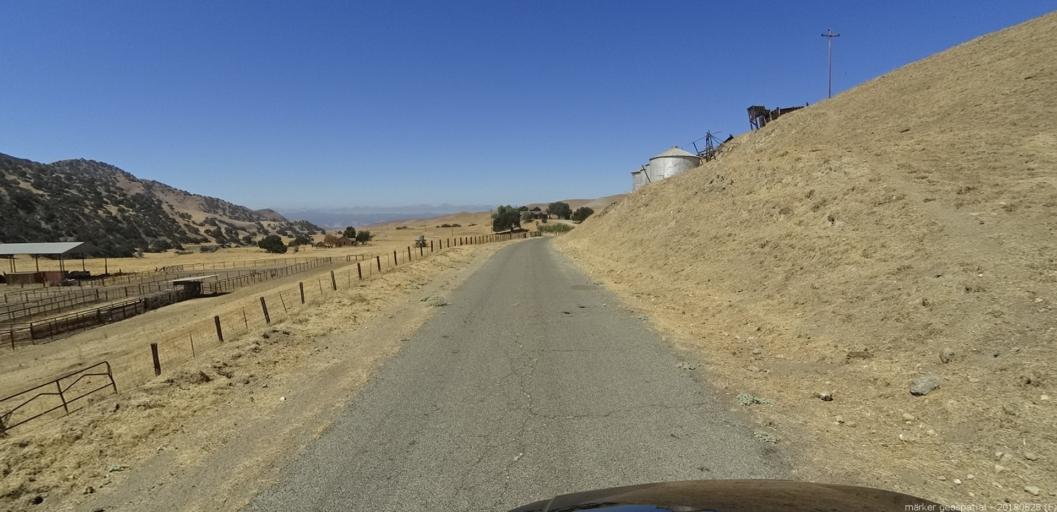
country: US
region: California
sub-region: San Luis Obispo County
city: San Miguel
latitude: 36.0675
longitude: -120.7799
